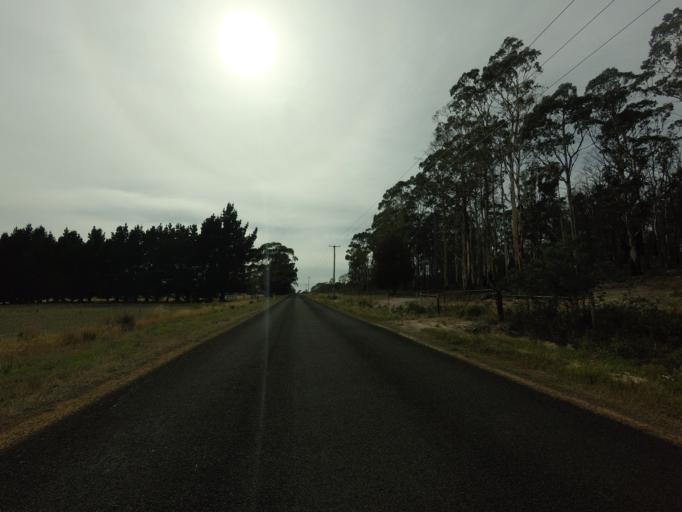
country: AU
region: Tasmania
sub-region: Sorell
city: Sorell
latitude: -42.4275
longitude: 147.4779
